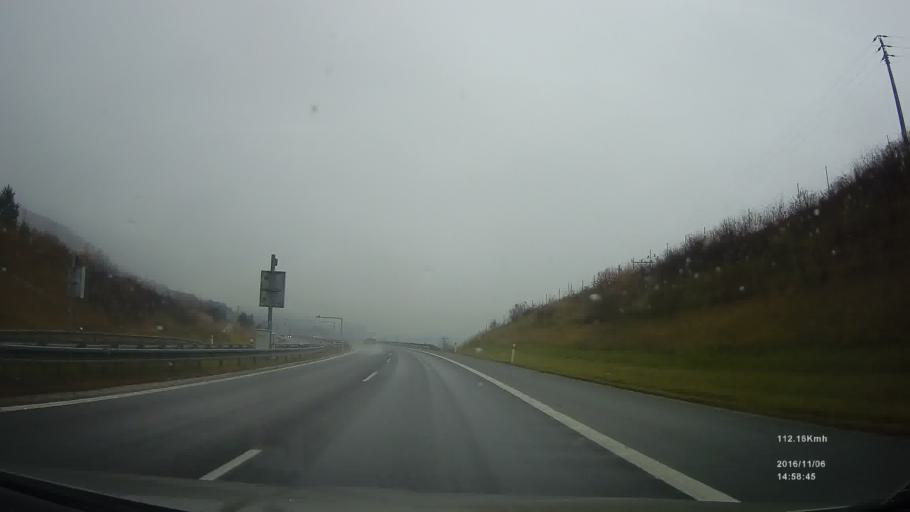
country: SK
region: Kosicky
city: Krompachy
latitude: 49.0149
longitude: 20.9541
